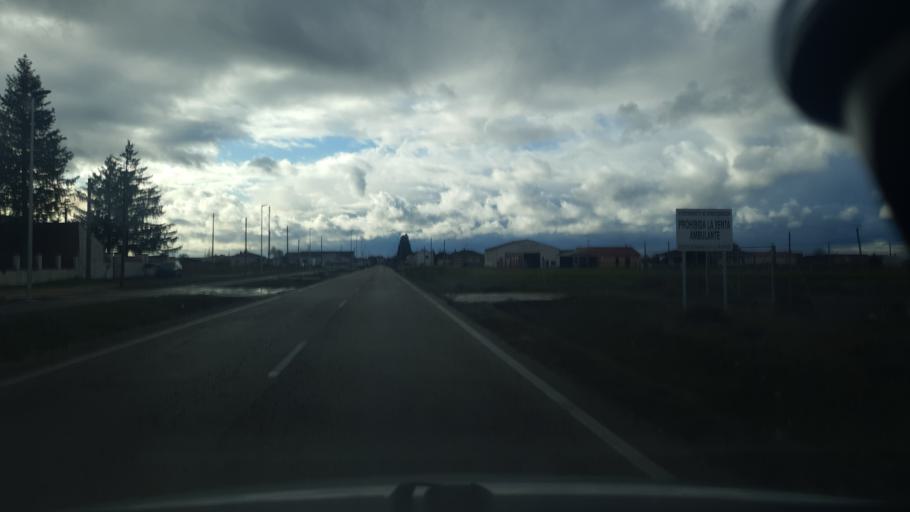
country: ES
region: Castille and Leon
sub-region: Provincia de Segovia
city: Sanchonuno
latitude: 41.2912
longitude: -4.3161
